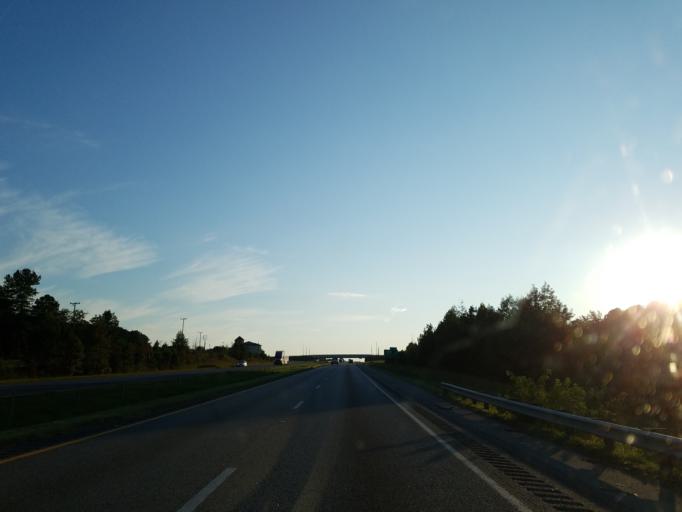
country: US
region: South Carolina
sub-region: Cherokee County
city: Gaffney
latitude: 35.0856
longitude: -81.7009
